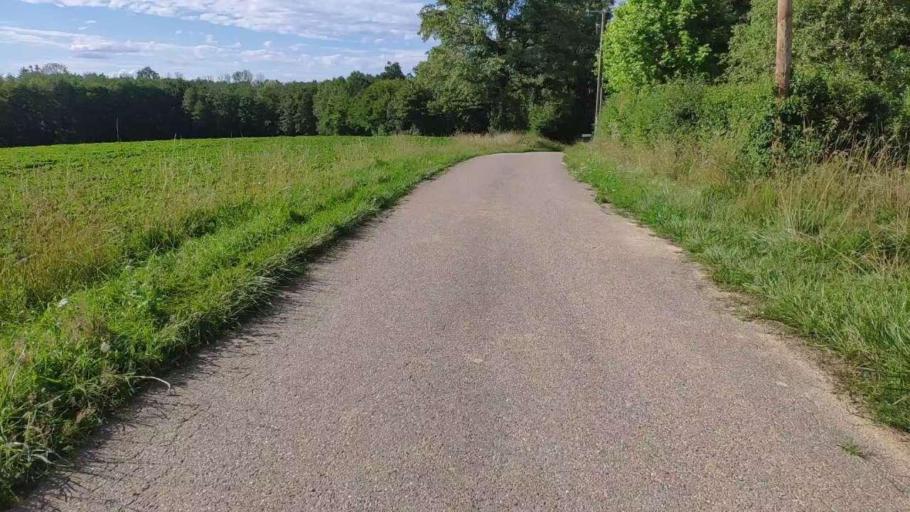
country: FR
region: Franche-Comte
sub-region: Departement du Jura
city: Bletterans
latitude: 46.8147
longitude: 5.4956
